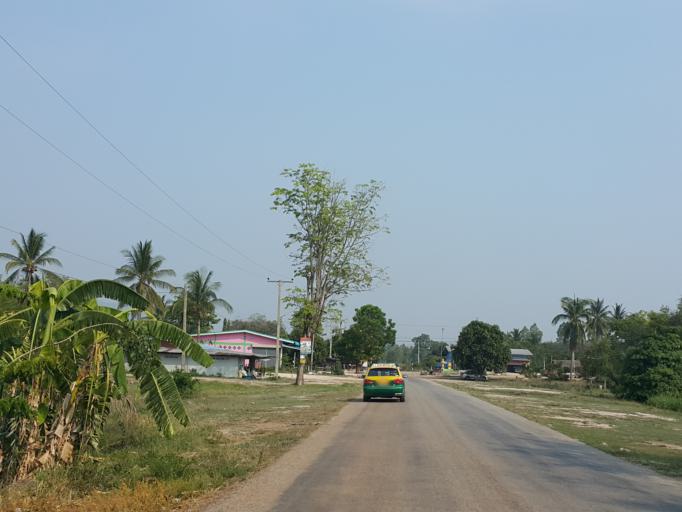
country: TH
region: Uthai Thani
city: Lan Sak
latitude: 15.3921
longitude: 99.5729
